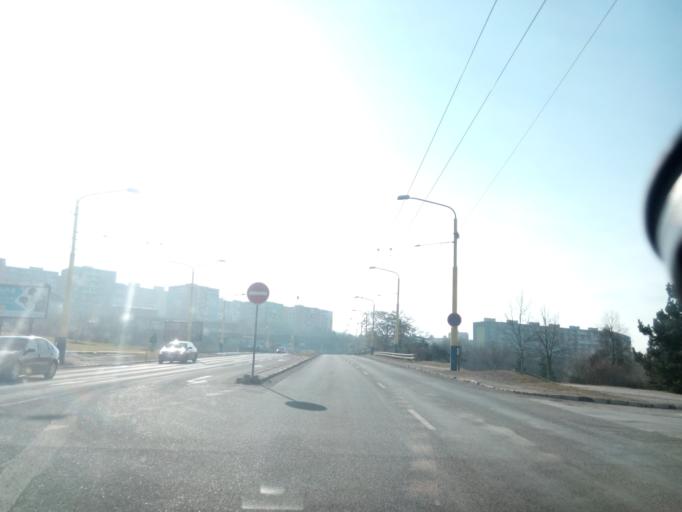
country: SK
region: Kosicky
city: Kosice
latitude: 48.7379
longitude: 21.2825
